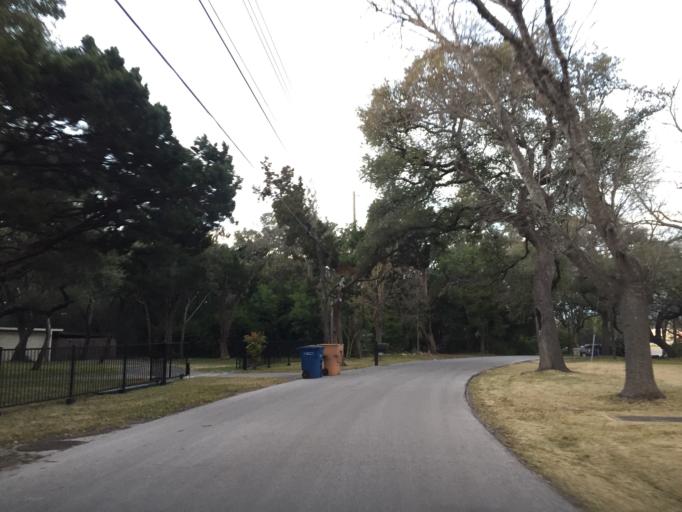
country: US
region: Texas
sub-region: Williamson County
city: Jollyville
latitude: 30.4264
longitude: -97.7488
